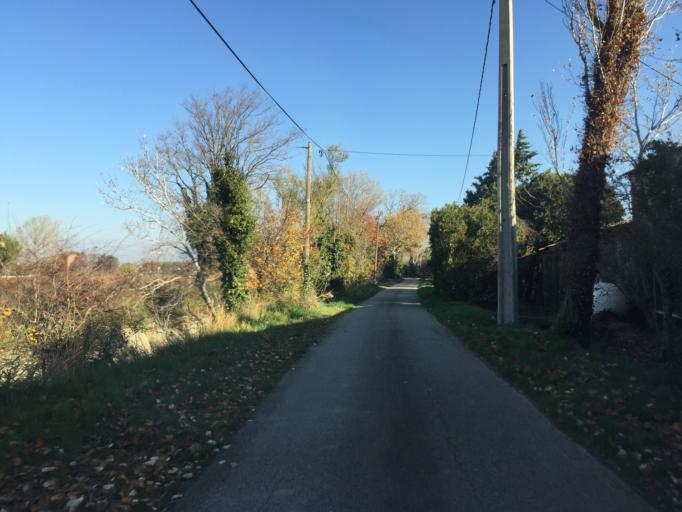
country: FR
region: Provence-Alpes-Cote d'Azur
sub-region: Departement du Vaucluse
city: Bedarrides
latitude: 44.0357
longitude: 4.9183
